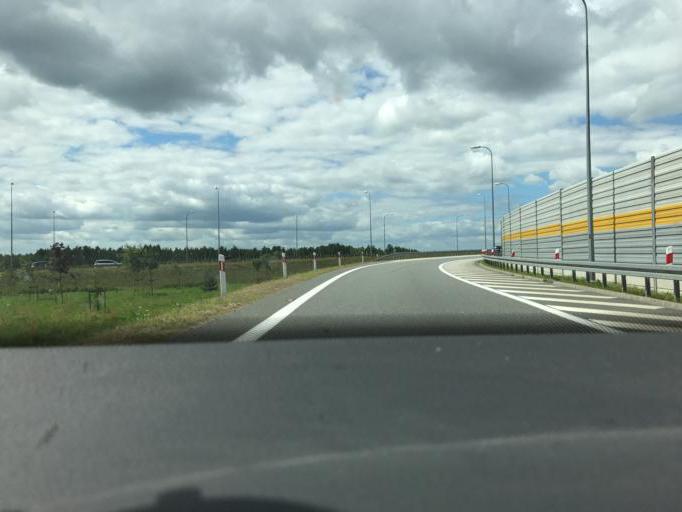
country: PL
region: Kujawsko-Pomorskie
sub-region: Powiat torunski
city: Lubicz Dolny
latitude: 53.0372
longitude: 18.7429
